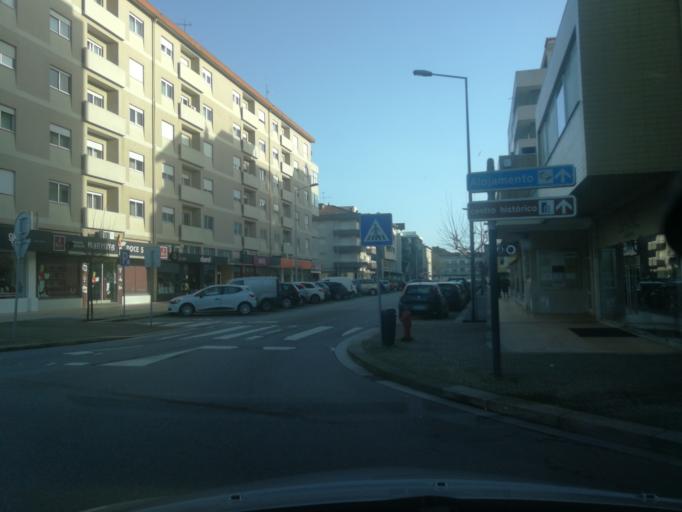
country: PT
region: Braga
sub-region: Barcelos
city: Barcelos
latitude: 41.5356
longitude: -8.6178
